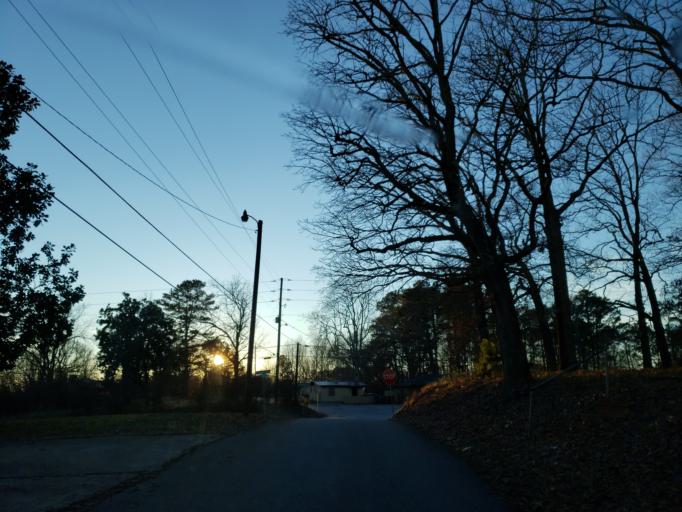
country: US
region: Georgia
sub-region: Paulding County
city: Hiram
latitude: 33.9050
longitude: -84.7720
